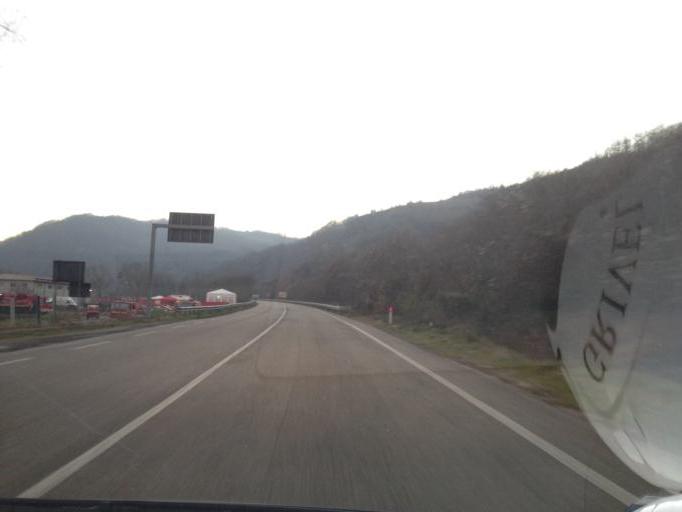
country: IT
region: The Marches
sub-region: Provincia di Ascoli Piceno
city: Arquata del Tronto
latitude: 42.7452
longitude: 13.2675
